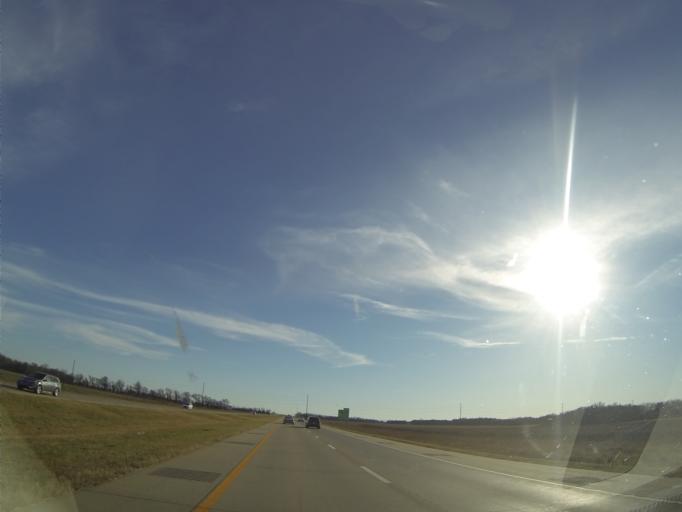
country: US
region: Kansas
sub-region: Saline County
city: Salina
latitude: 38.7505
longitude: -97.6182
